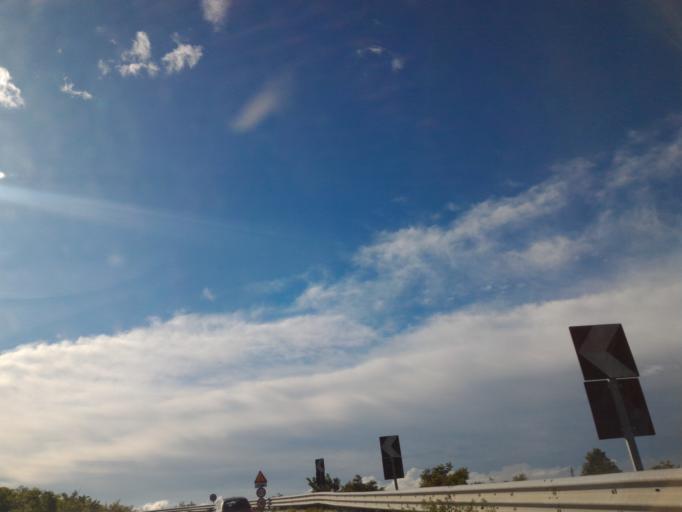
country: IT
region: Piedmont
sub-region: Provincia di Cuneo
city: Trinita
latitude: 44.4693
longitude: 7.7687
